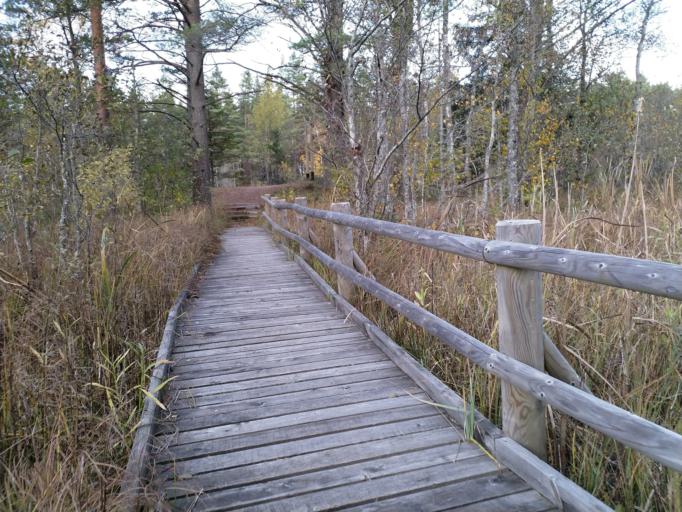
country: LV
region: Dundaga
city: Dundaga
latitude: 57.6485
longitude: 22.2575
